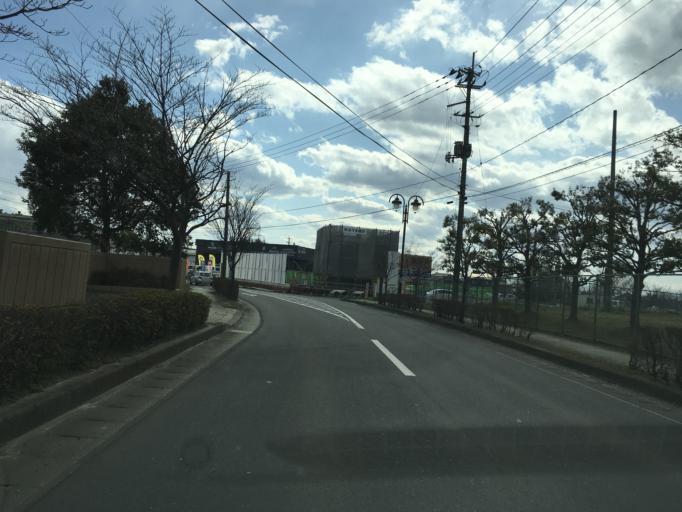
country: JP
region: Miyagi
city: Wakuya
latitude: 38.6975
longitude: 141.2088
